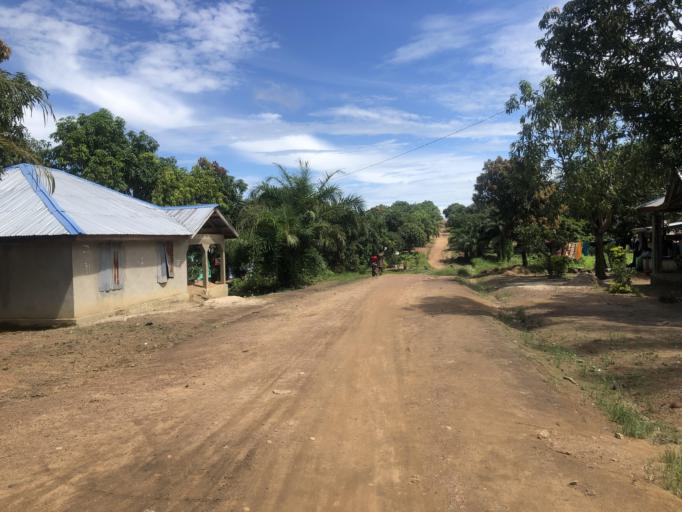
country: SL
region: Eastern Province
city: Koidu
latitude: 8.6382
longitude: -10.9480
